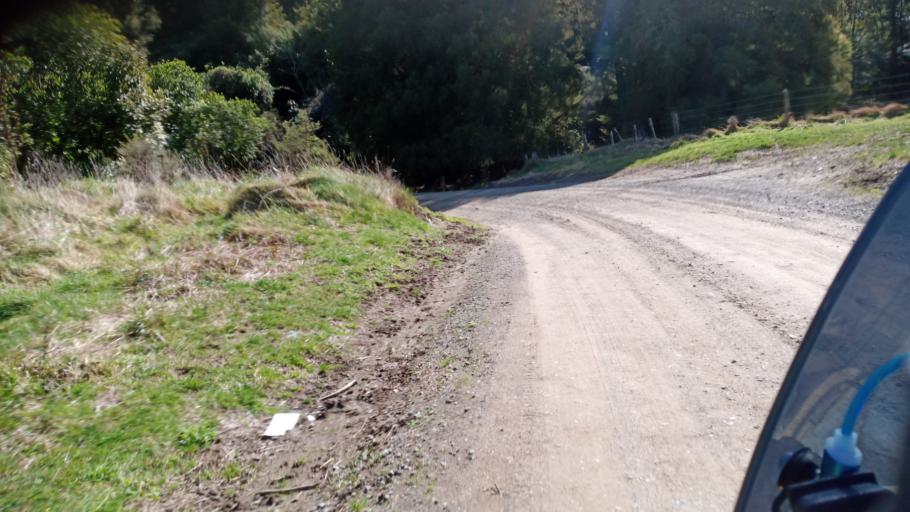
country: NZ
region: Hawke's Bay
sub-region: Wairoa District
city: Wairoa
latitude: -38.8188
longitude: 177.1604
